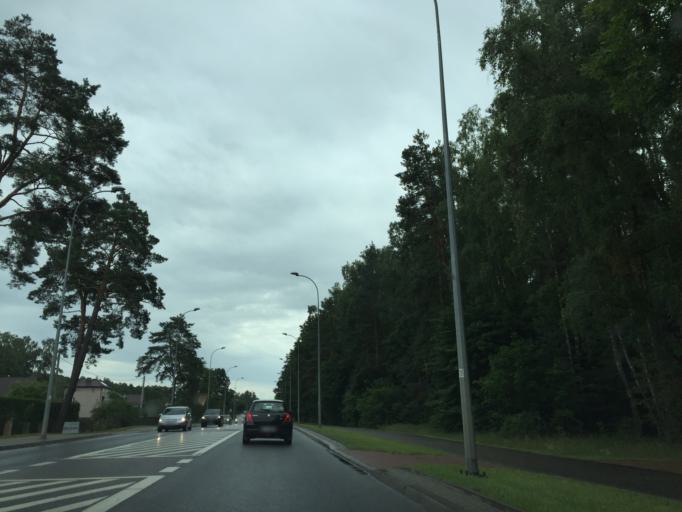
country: PL
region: Podlasie
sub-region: Bialystok
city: Bialystok
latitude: 53.1023
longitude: 23.2227
